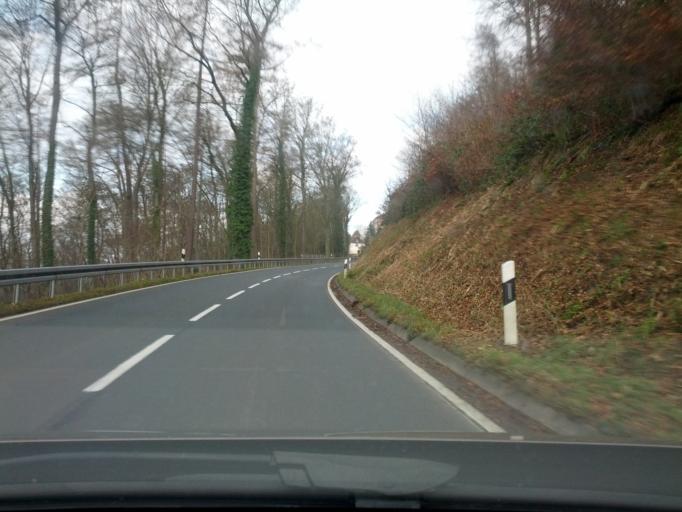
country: DE
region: Lower Saxony
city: Furstenberg
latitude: 51.7263
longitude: 9.3990
